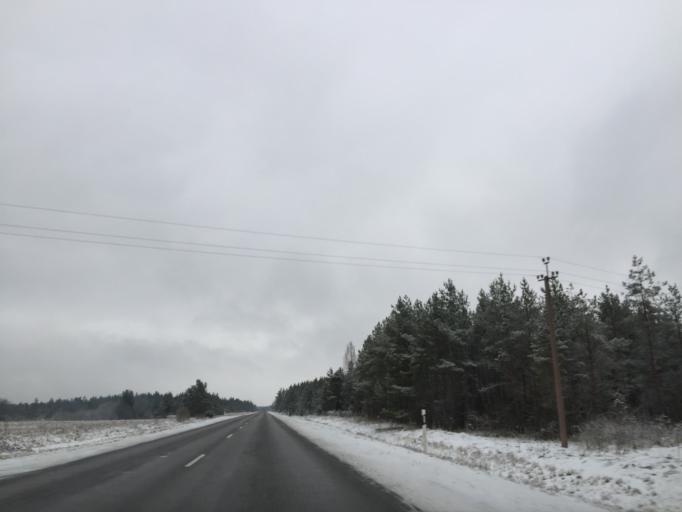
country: EE
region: Laeaene
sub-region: Lihula vald
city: Lihula
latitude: 58.6209
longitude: 23.9036
